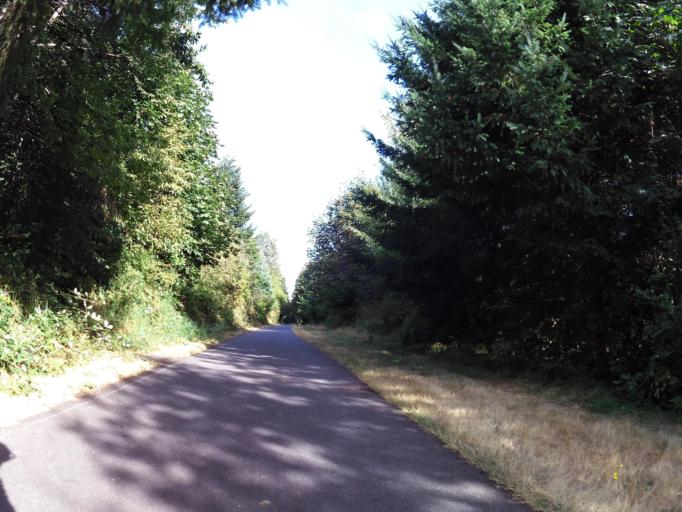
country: US
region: Washington
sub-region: Thurston County
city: Olympia
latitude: 47.0398
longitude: -122.8650
